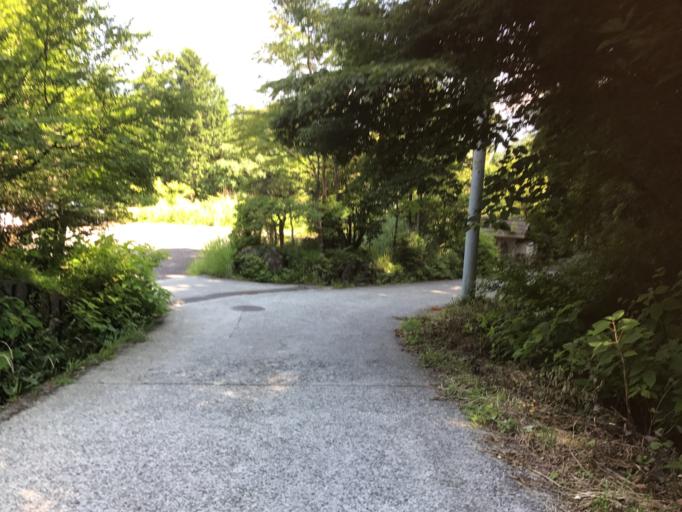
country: JP
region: Kanagawa
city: Hakone
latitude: 35.2542
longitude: 139.0001
